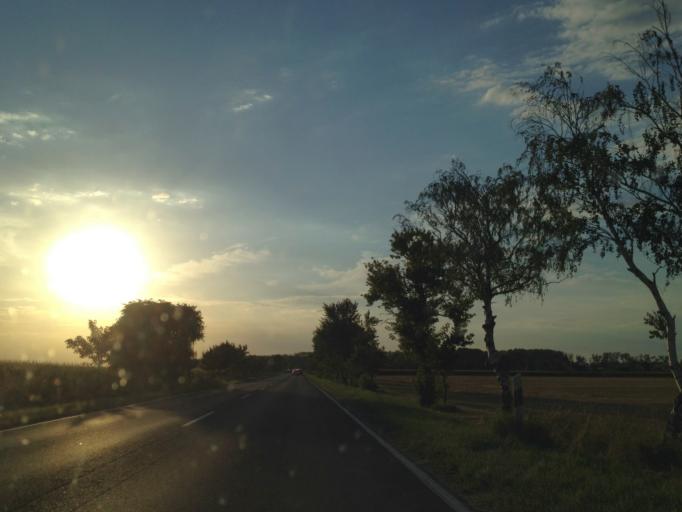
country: HU
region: Gyor-Moson-Sopron
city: Kimle
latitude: 47.8081
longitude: 17.3661
